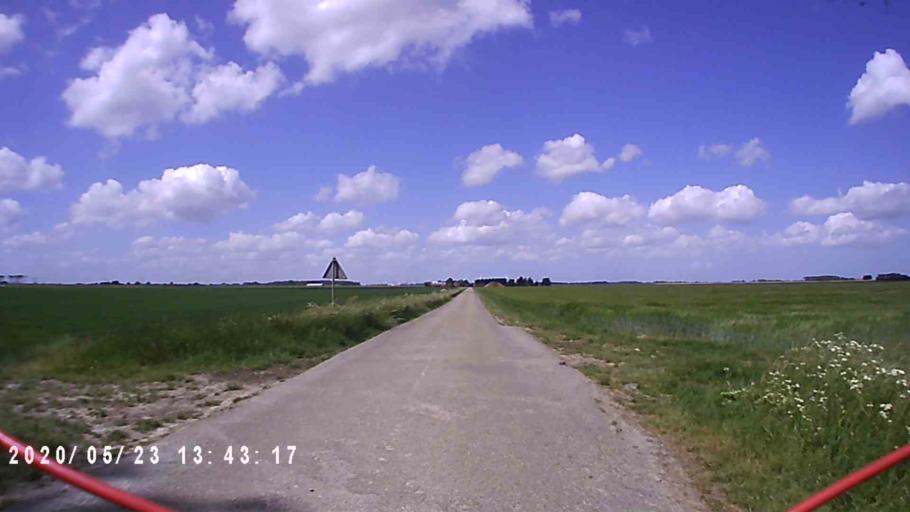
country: NL
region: Groningen
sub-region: Gemeente  Oldambt
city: Winschoten
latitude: 53.2637
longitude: 7.0706
